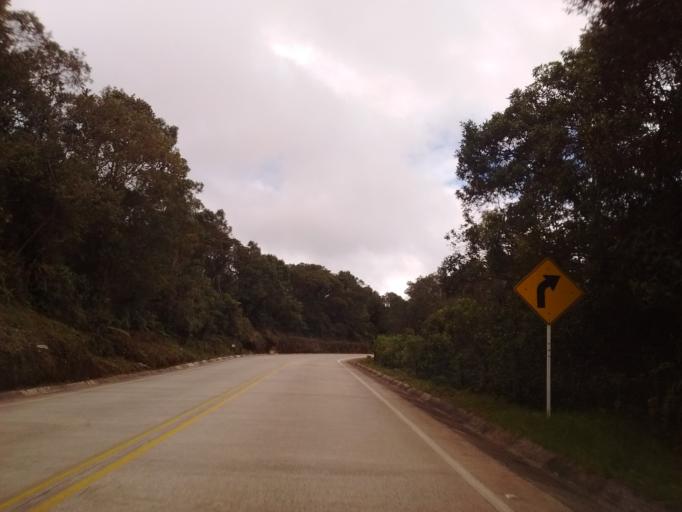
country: CO
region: Huila
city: Isnos
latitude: 2.0489
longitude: -76.3100
